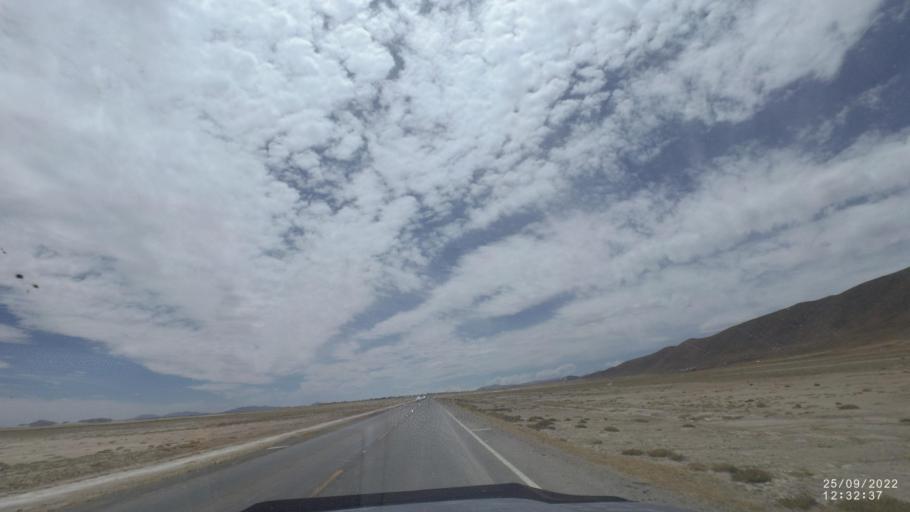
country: BO
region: Oruro
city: Machacamarca
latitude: -18.2086
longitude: -67.0102
